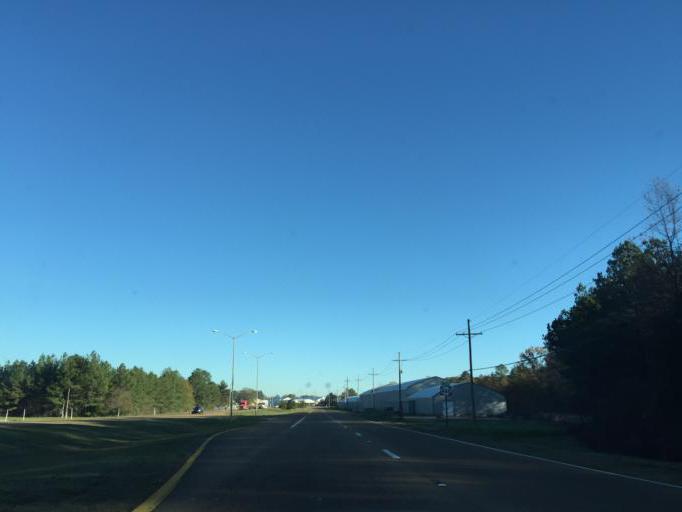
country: US
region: Mississippi
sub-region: Rankin County
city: Flowood
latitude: 32.2973
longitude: -90.1436
